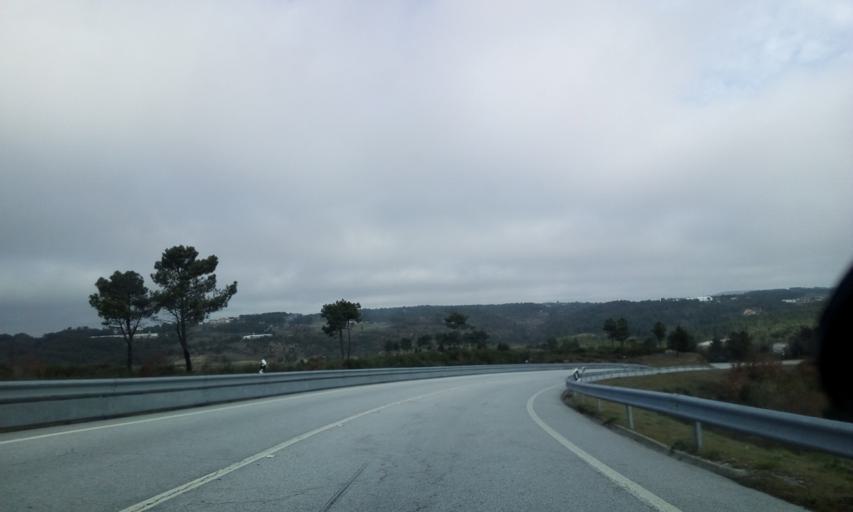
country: PT
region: Guarda
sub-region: Aguiar da Beira
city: Aguiar da Beira
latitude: 40.7719
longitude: -7.5045
